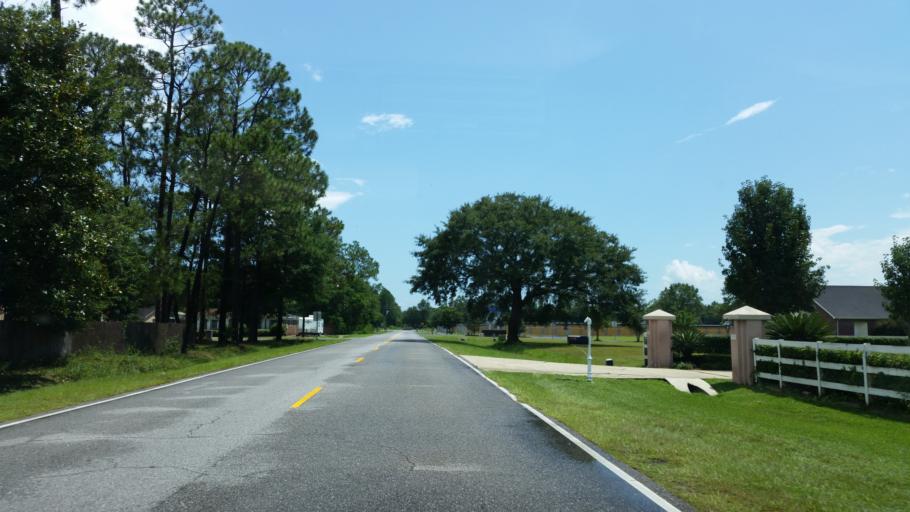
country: US
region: Florida
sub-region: Escambia County
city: Ensley
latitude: 30.5370
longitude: -87.3005
